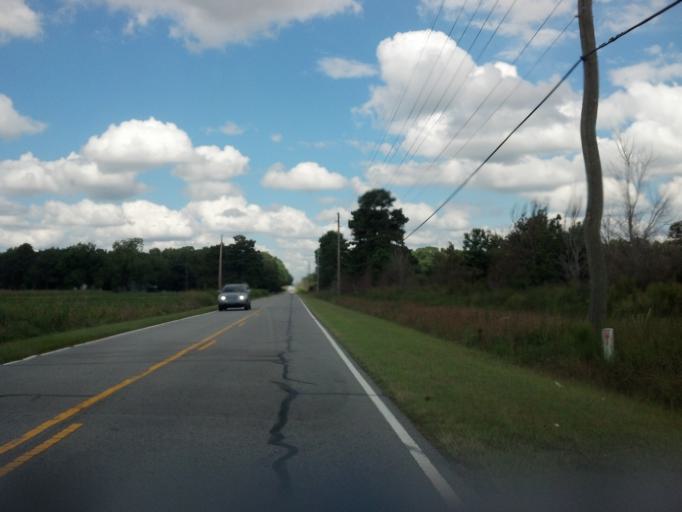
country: US
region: North Carolina
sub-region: Pitt County
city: Ayden
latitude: 35.5014
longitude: -77.4132
